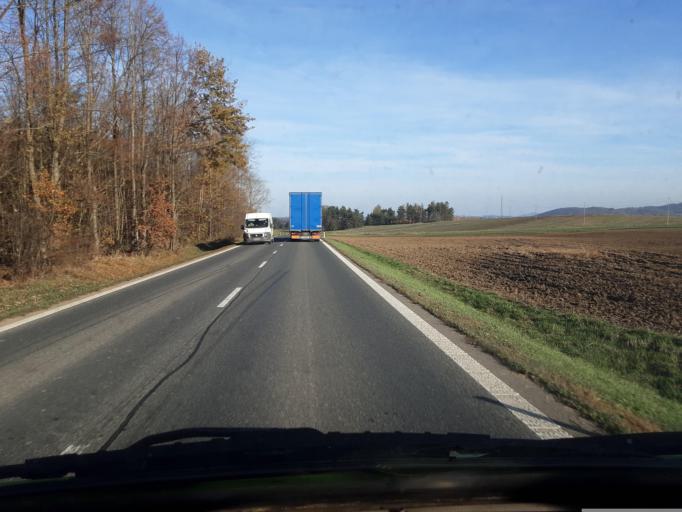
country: CZ
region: Plzensky
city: Horazd'ovice
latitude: 49.3255
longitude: 13.6209
